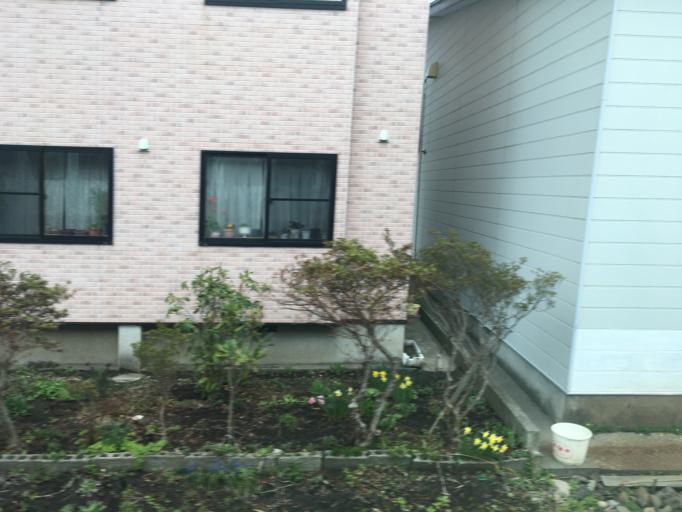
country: JP
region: Aomori
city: Shimokizukuri
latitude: 40.7772
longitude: 140.2227
